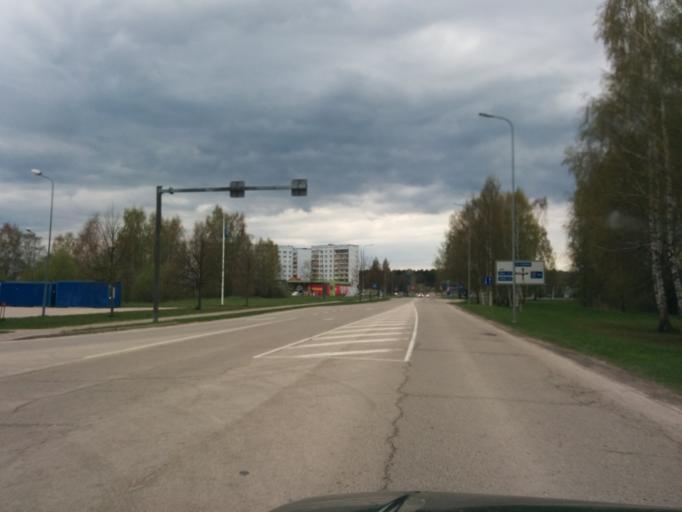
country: LV
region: Ozolnieku
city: Ozolnieki
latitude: 56.6690
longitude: 23.7653
